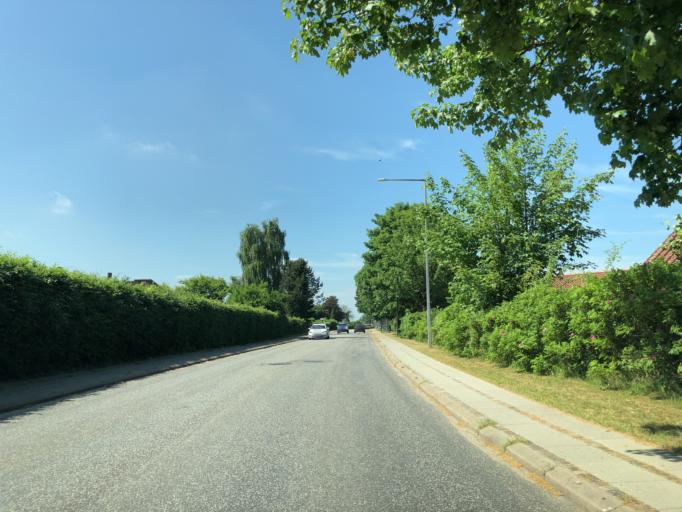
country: DK
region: South Denmark
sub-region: Kolding Kommune
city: Kolding
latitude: 55.5211
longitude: 9.4751
